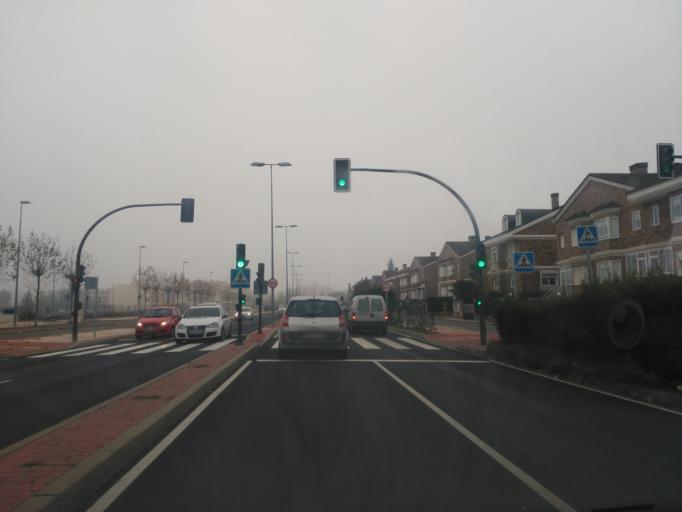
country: ES
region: Castille and Leon
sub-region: Provincia de Salamanca
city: Santa Marta de Tormes
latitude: 40.9541
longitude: -5.6422
